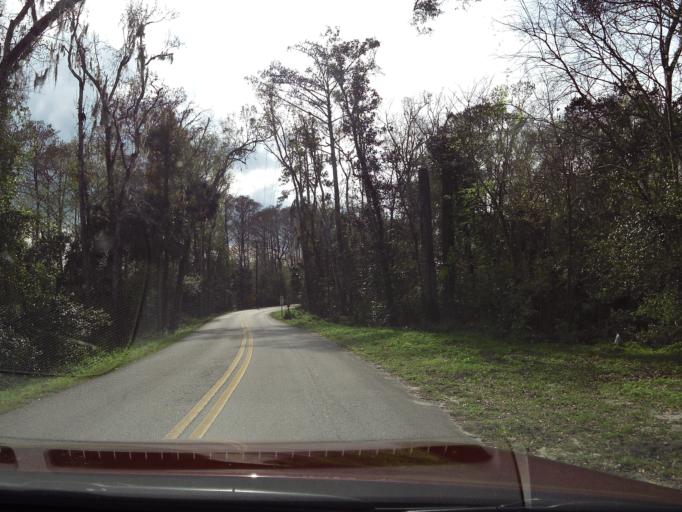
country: US
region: Florida
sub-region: Volusia County
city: De Leon Springs
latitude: 29.1515
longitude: -81.3029
